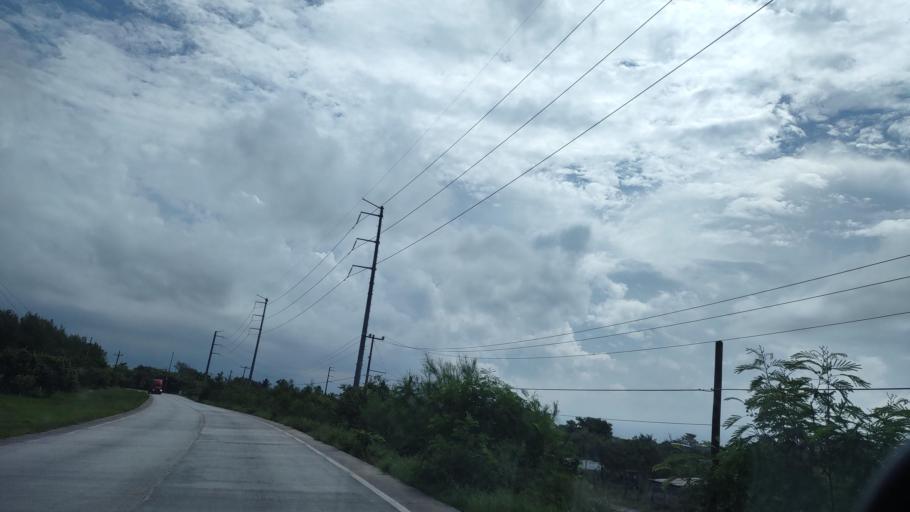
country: MX
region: Veracruz
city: Anahuac
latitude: 22.2069
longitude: -97.8684
